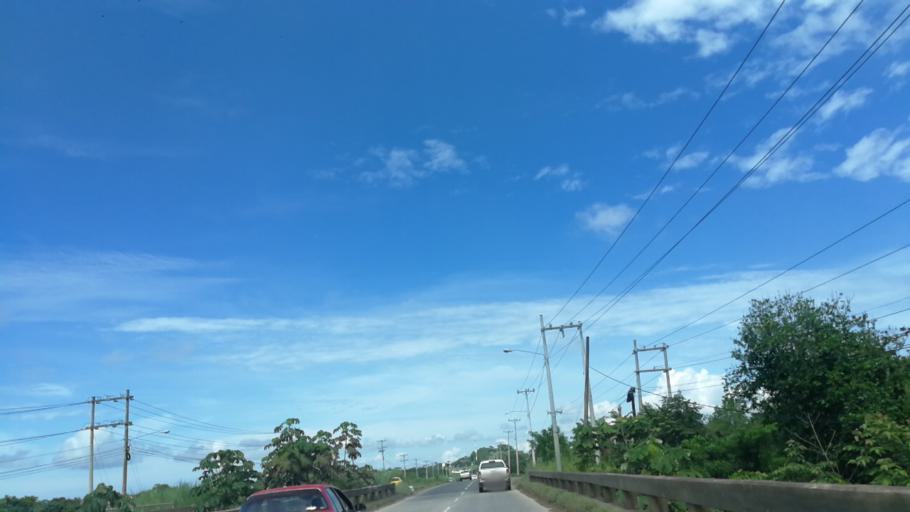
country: PA
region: Panama
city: Los Lotes
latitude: 9.1018
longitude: -79.2774
